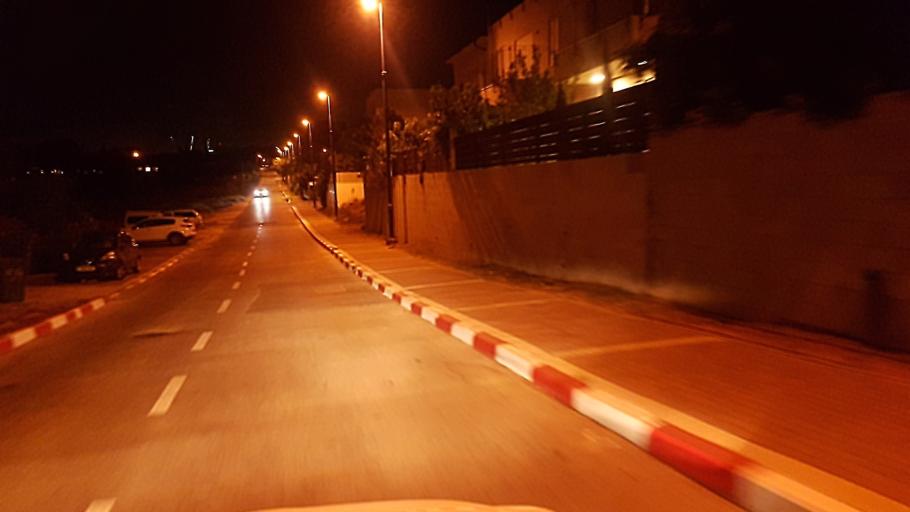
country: IL
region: Central District
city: Hod HaSharon
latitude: 32.1639
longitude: 34.8899
